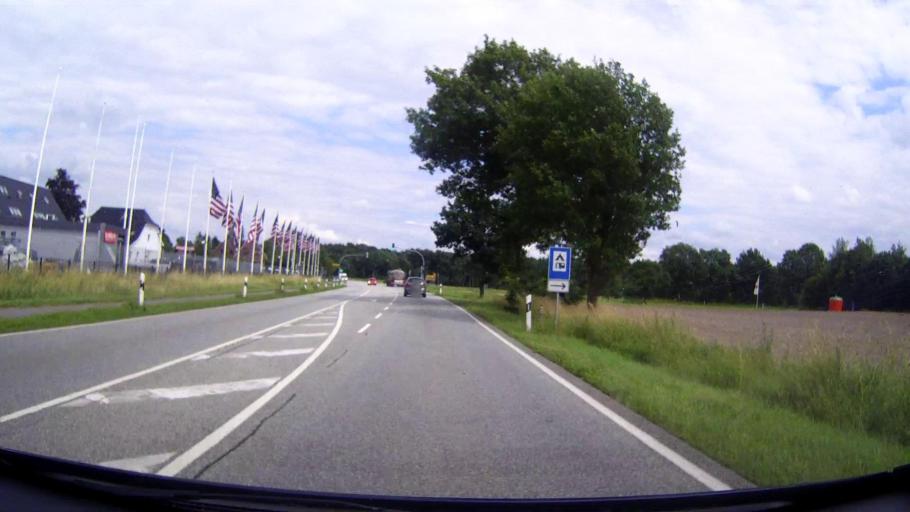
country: DE
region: Schleswig-Holstein
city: Wasbek
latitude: 54.0684
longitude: 9.8926
